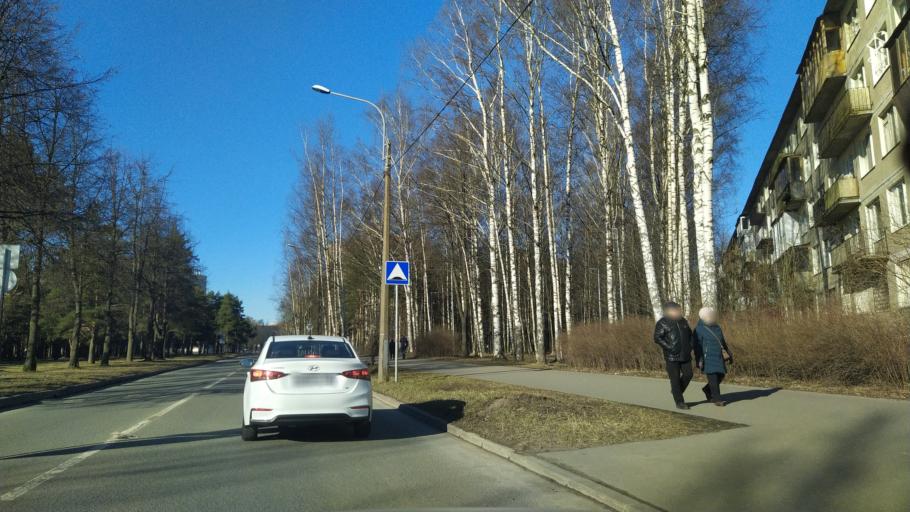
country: RU
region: Leningrad
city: Akademicheskoe
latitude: 60.0018
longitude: 30.4220
